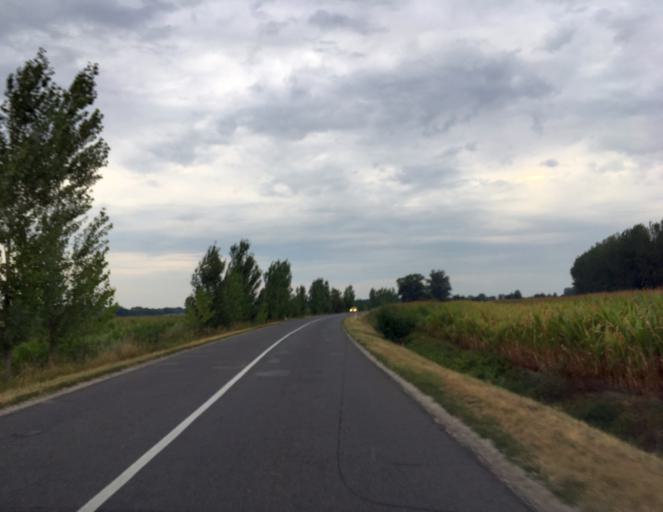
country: SK
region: Trnavsky
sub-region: Okres Dunajska Streda
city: Velky Meder
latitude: 47.8998
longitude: 17.6793
